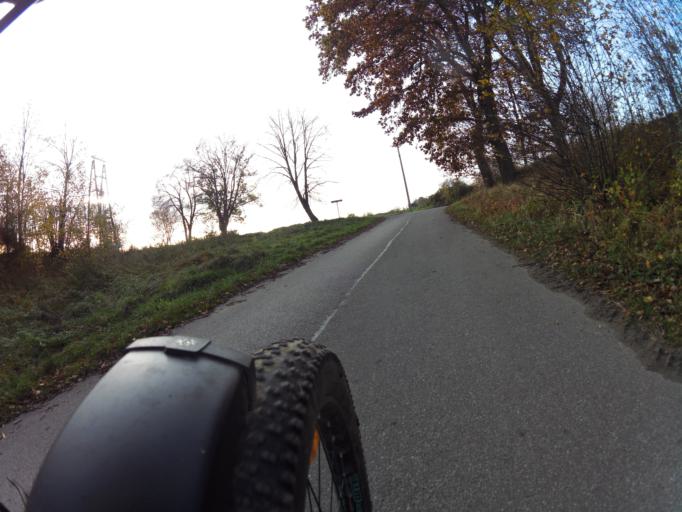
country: PL
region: Pomeranian Voivodeship
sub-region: Powiat pucki
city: Krokowa
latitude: 54.7514
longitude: 18.1842
